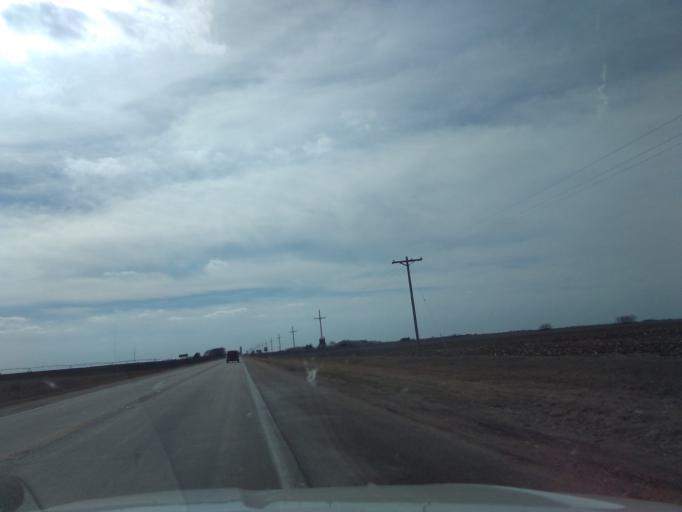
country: US
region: Nebraska
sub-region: Gage County
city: Beatrice
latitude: 40.2095
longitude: -96.9355
